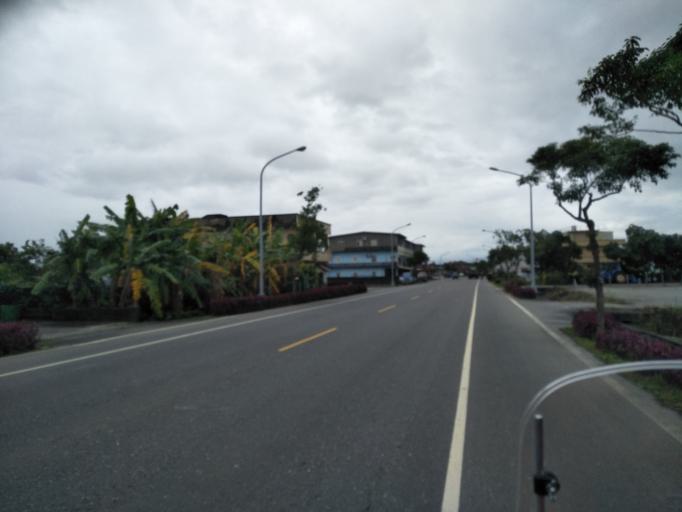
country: TW
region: Taiwan
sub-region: Yilan
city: Yilan
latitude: 24.7942
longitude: 121.7852
